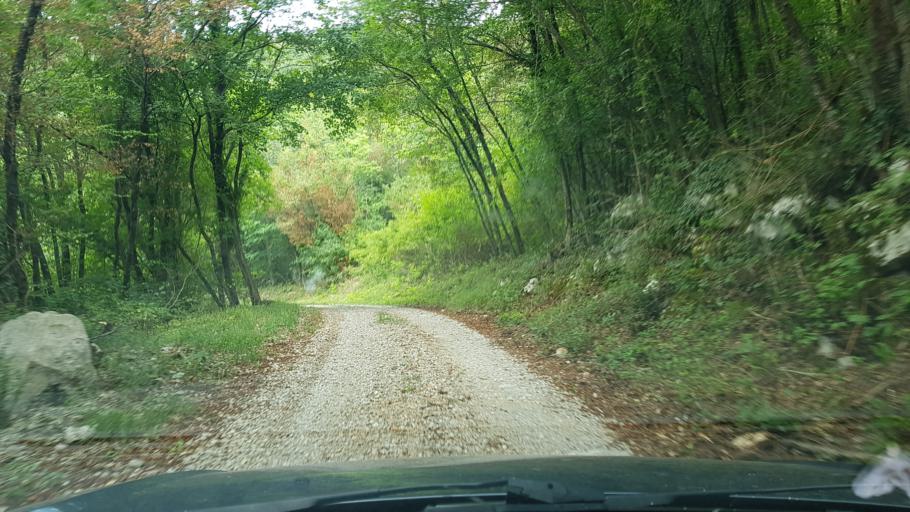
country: SI
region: Kanal
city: Deskle
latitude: 46.0155
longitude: 13.6266
